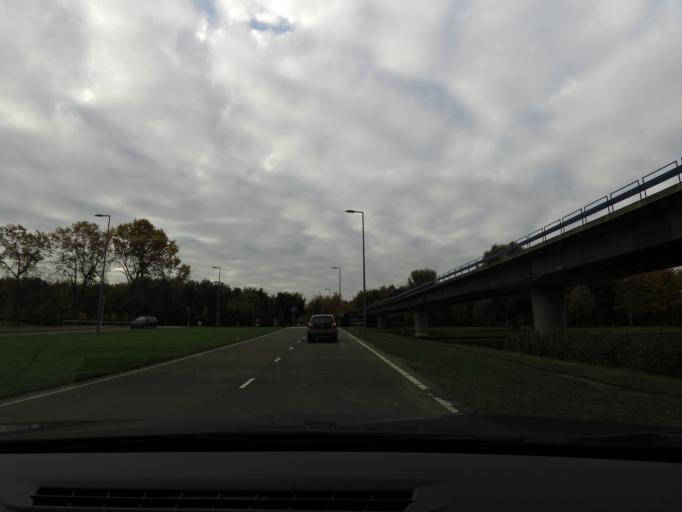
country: NL
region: South Holland
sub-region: Gemeente Rotterdam
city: Delfshaven
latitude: 51.8806
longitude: 4.4798
